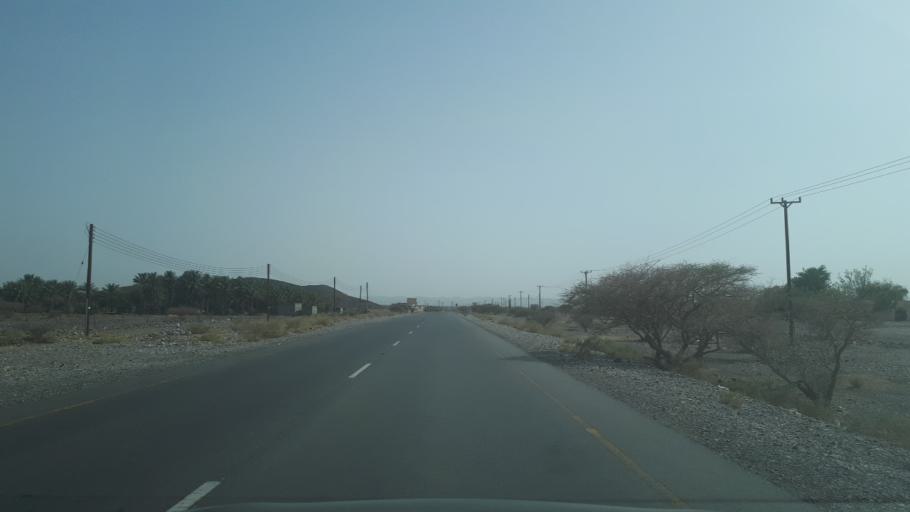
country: OM
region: Az Zahirah
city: `Ibri
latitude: 23.1164
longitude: 56.8808
